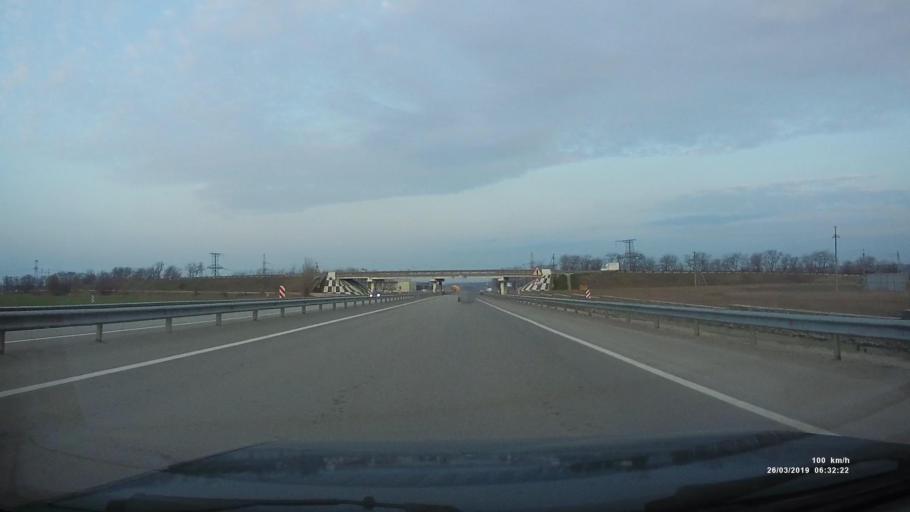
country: RU
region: Rostov
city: Kalinin
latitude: 47.2713
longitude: 39.5126
